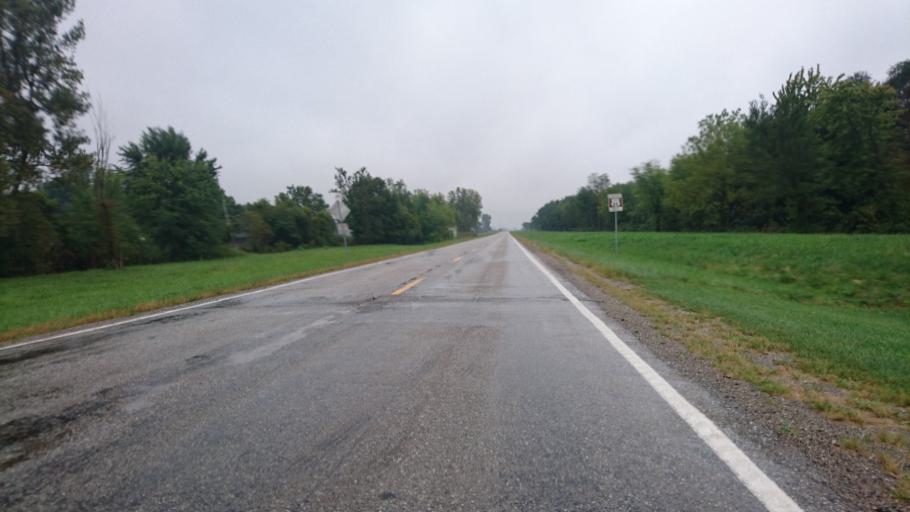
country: US
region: Illinois
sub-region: Sangamon County
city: Williamsville
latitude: 40.0199
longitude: -89.4853
